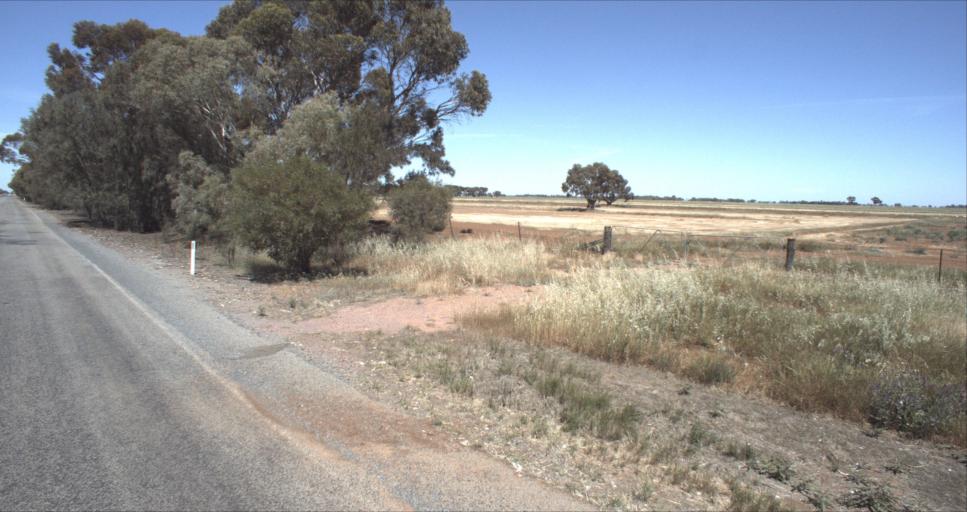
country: AU
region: New South Wales
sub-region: Leeton
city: Leeton
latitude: -34.4681
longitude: 146.2929
